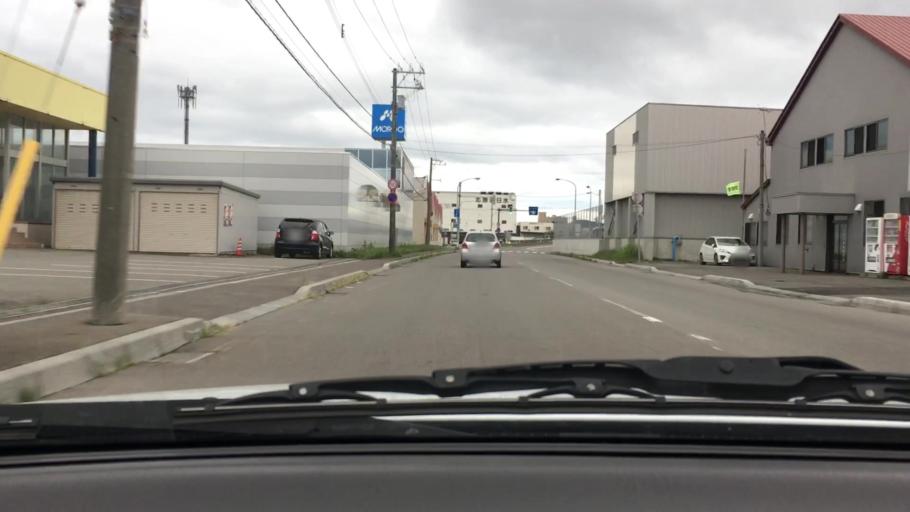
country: JP
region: Hokkaido
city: Hakodate
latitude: 41.7874
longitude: 140.7282
